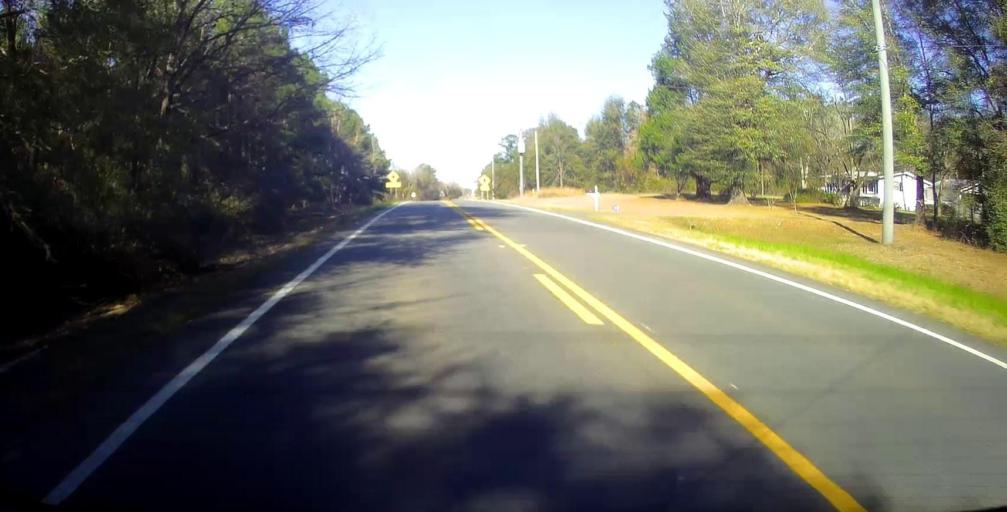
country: US
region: Georgia
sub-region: Macon County
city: Oglethorpe
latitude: 32.2362
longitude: -84.0952
